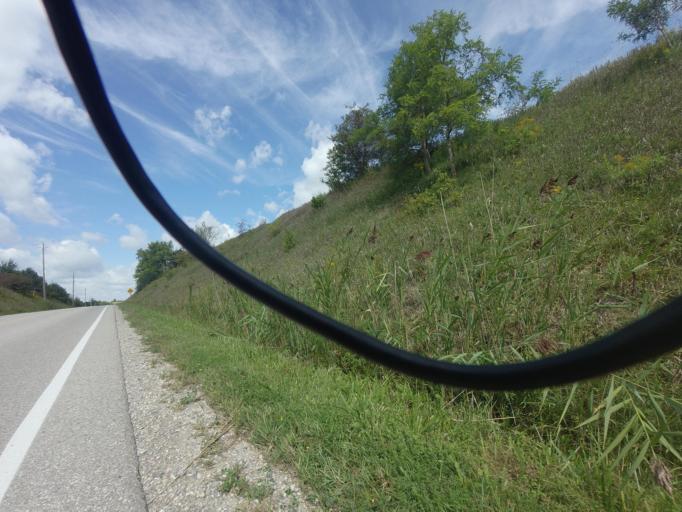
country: CA
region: Ontario
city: Stratford
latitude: 43.5168
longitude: -80.8459
